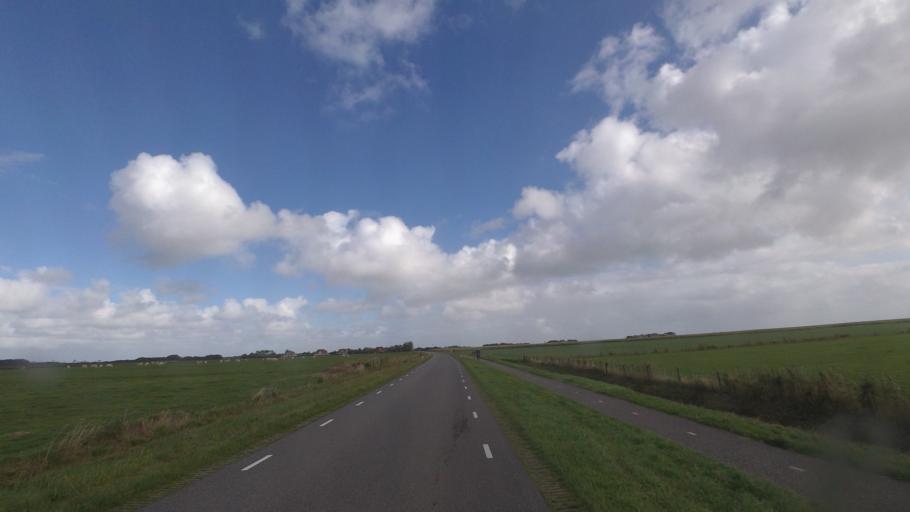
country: NL
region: Friesland
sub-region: Gemeente Ameland
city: Hollum
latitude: 53.4378
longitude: 5.6462
